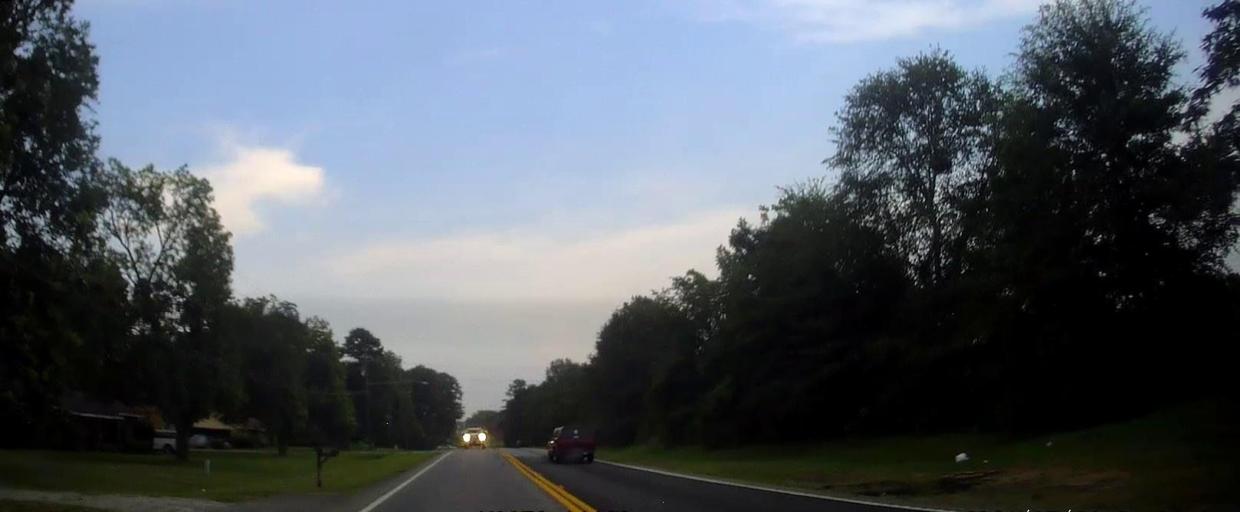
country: US
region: Georgia
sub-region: Laurens County
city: East Dublin
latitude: 32.5541
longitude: -82.8627
